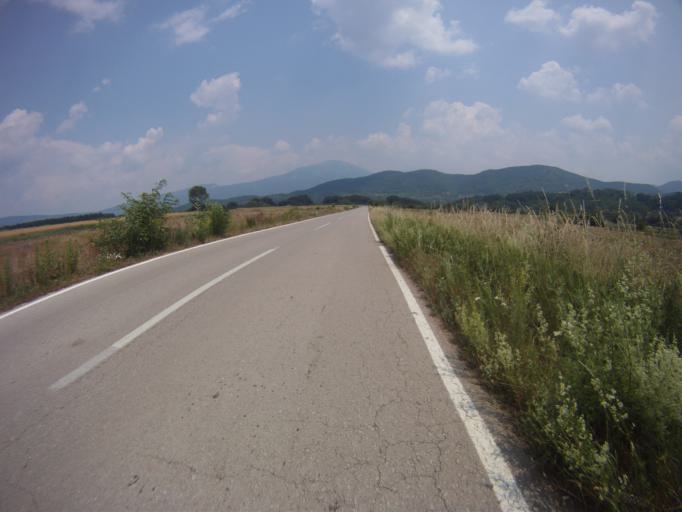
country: RS
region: Central Serbia
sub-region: Nisavski Okrug
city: Gadzin Han
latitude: 43.2068
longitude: 22.0081
